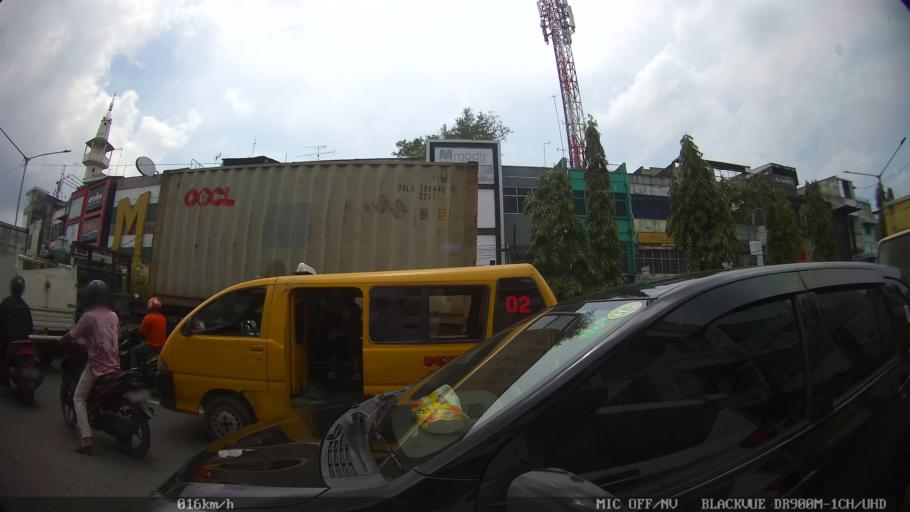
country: ID
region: North Sumatra
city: Medan
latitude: 3.6295
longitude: 98.6696
